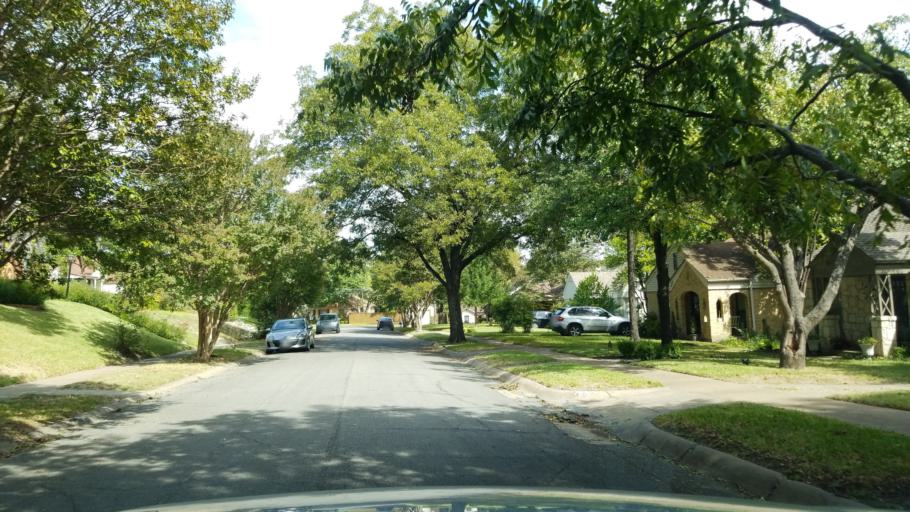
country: US
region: Texas
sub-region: Dallas County
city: Highland Park
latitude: 32.8048
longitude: -96.7371
